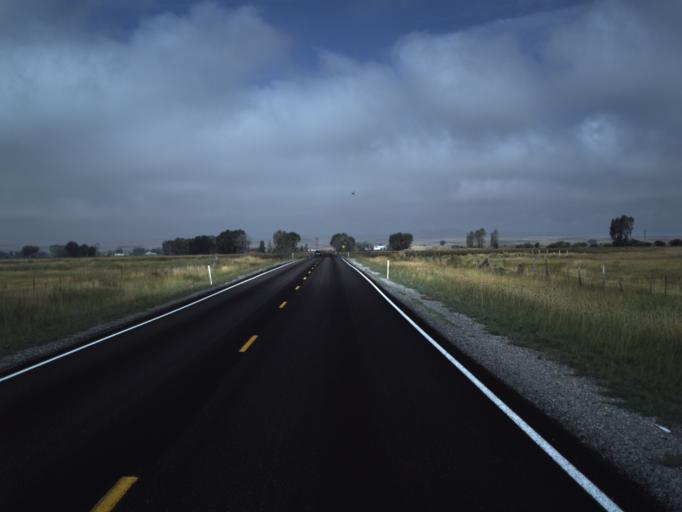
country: US
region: Utah
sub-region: Rich County
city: Randolph
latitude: 41.5134
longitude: -111.1341
